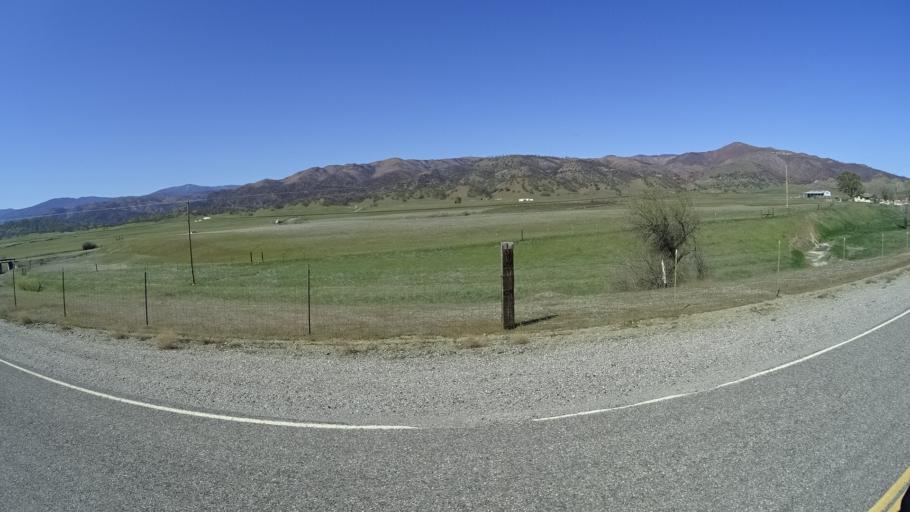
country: US
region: California
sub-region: Tehama County
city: Rancho Tehama Reserve
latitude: 39.7005
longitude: -122.5499
